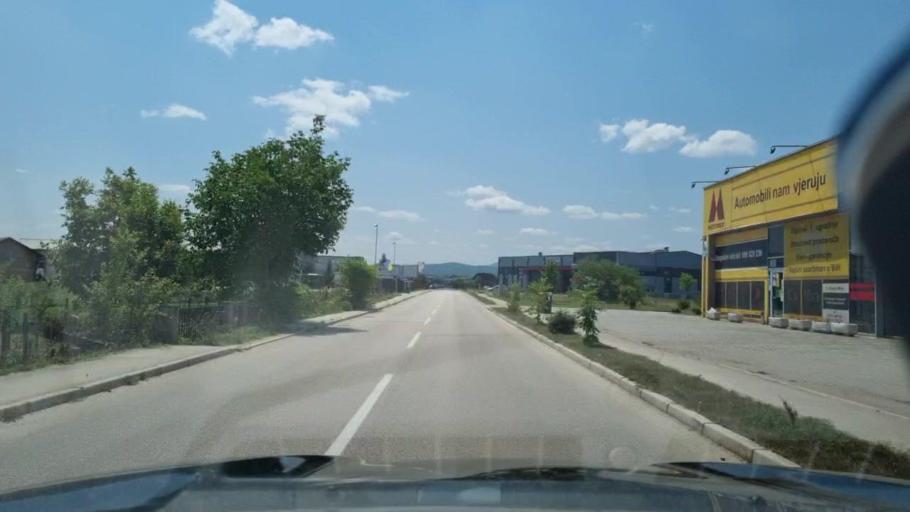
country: BA
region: Federation of Bosnia and Herzegovina
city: Sanski Most
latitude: 44.7533
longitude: 16.6745
